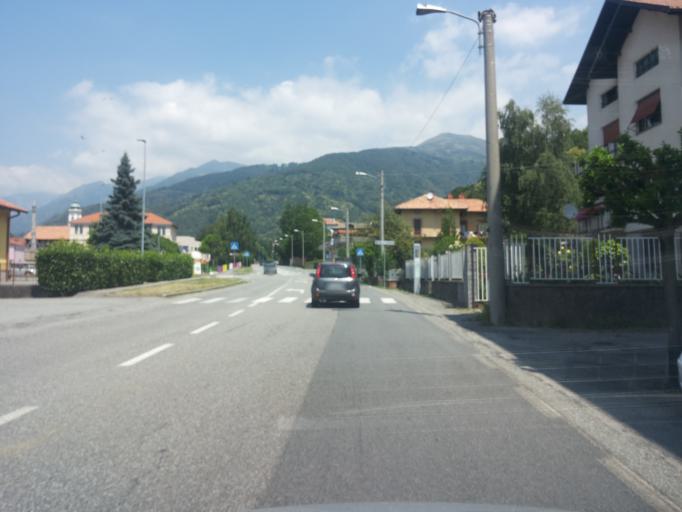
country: IT
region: Piedmont
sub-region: Provincia di Biella
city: Sagliano Micca
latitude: 45.6215
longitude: 8.0463
